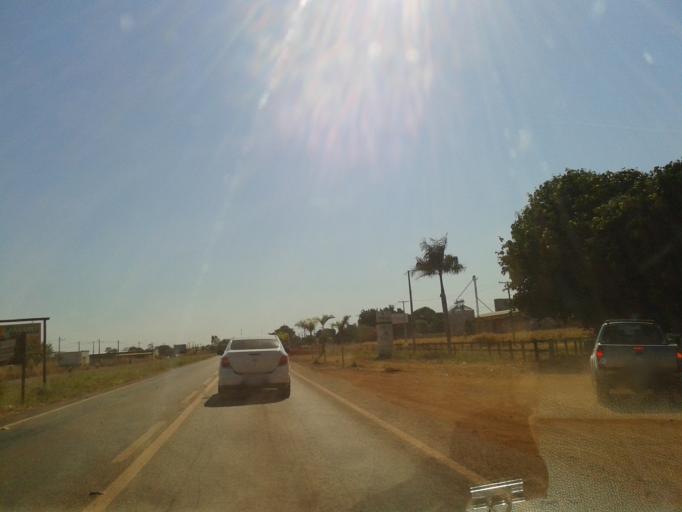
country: BR
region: Goias
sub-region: Crixas
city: Crixas
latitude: -14.1155
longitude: -50.3444
